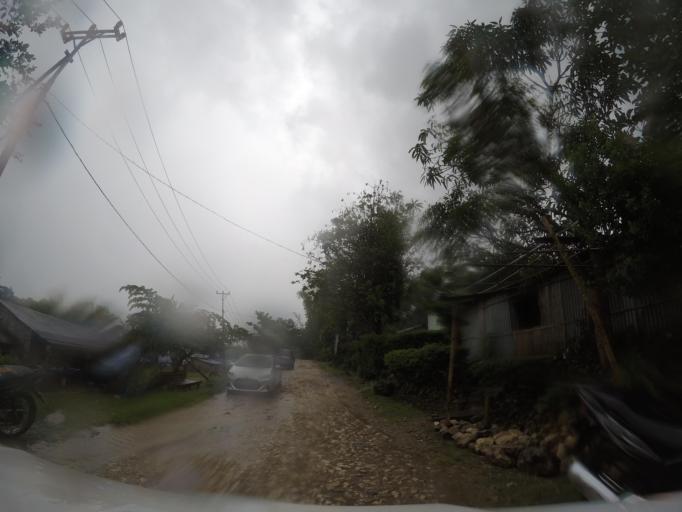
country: TL
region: Baucau
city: Venilale
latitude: -8.6427
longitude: 126.3981
